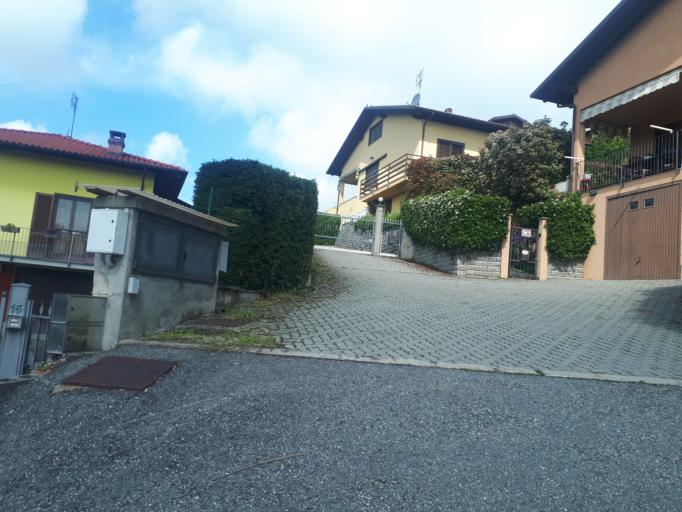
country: IT
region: Piedmont
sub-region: Provincia di Torino
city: Vialfre
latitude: 45.3793
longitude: 7.8201
